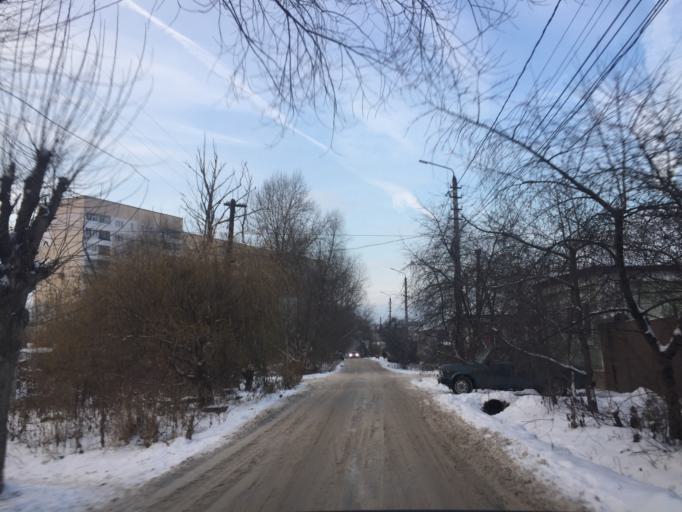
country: RU
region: Tula
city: Tula
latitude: 54.1978
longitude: 37.6794
